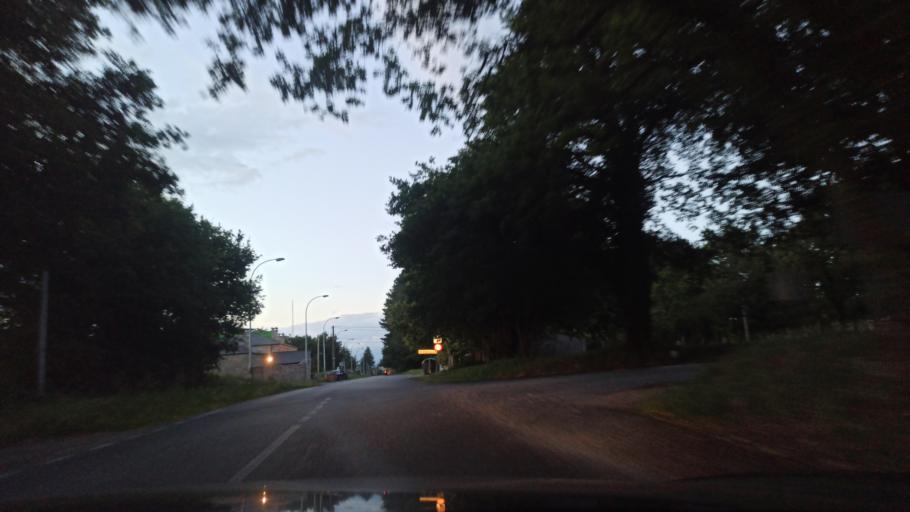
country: ES
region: Galicia
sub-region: Provincia de Lugo
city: Lugo
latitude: 42.9850
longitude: -7.5825
